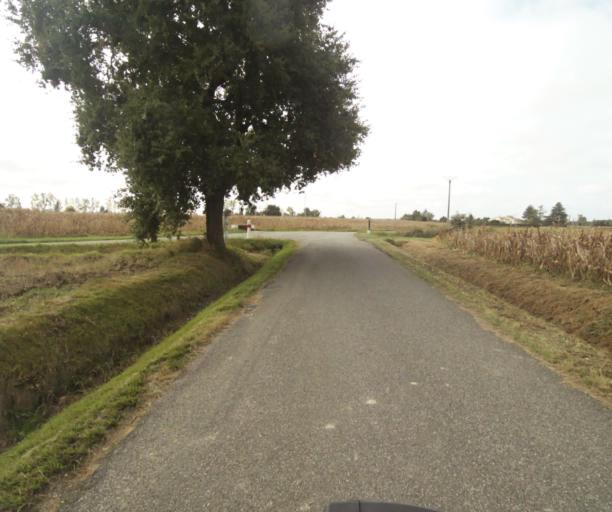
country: FR
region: Midi-Pyrenees
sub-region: Departement du Tarn-et-Garonne
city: Finhan
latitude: 43.9179
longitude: 1.2409
